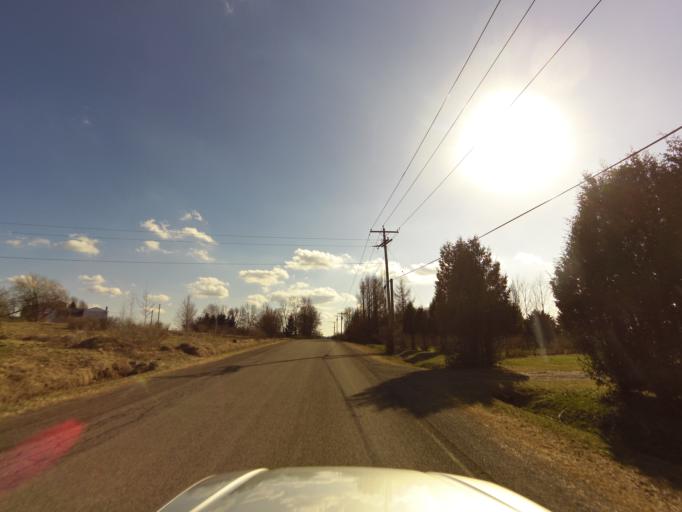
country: US
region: New York
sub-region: Allegany County
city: Houghton
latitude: 42.4385
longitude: -78.3059
